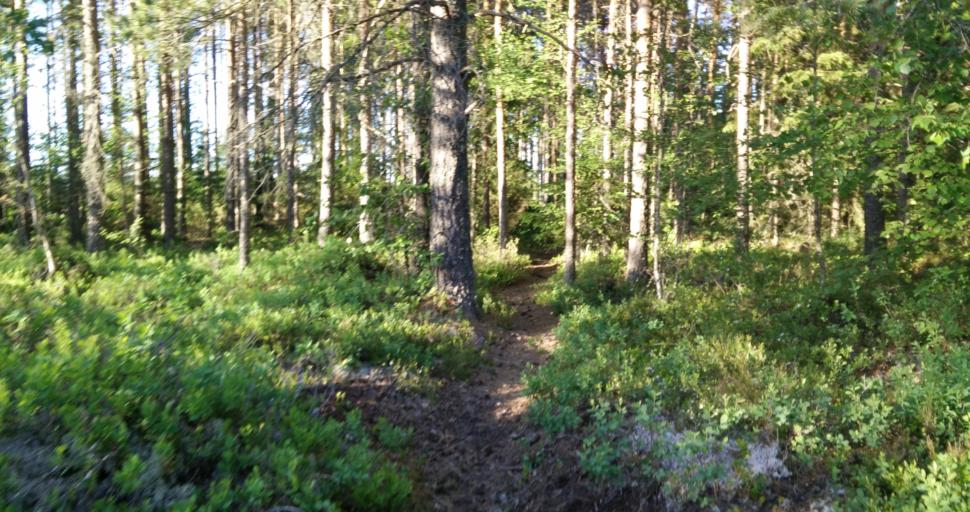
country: SE
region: Vaermland
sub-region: Hagfors Kommun
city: Hagfors
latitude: 60.0207
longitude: 13.5829
